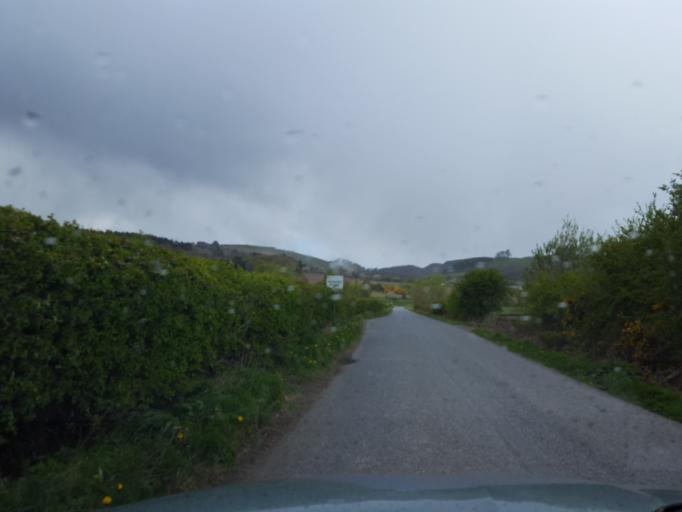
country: GB
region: Scotland
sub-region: Perth and Kinross
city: Errol
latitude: 56.4218
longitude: -3.2422
